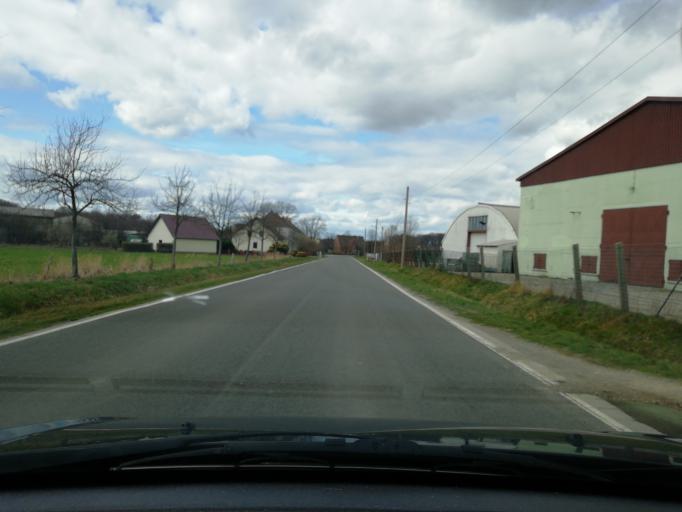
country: DE
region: Brandenburg
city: Altdobern
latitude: 51.7106
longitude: 14.0496
